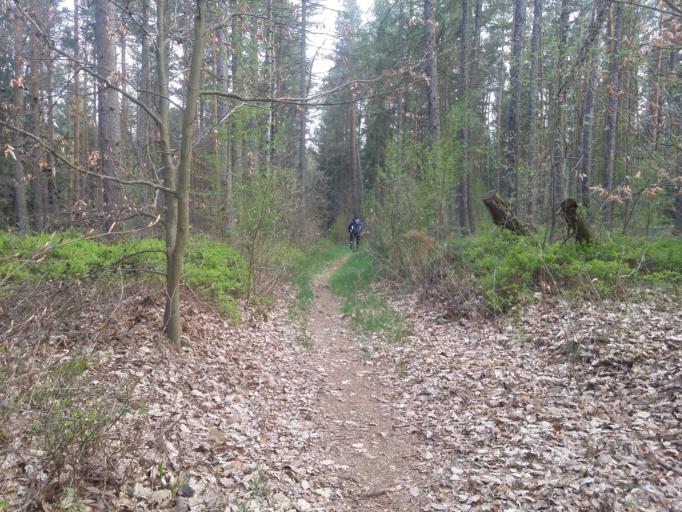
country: DE
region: Saxony-Anhalt
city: Bad Suderode
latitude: 51.7202
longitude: 11.0946
